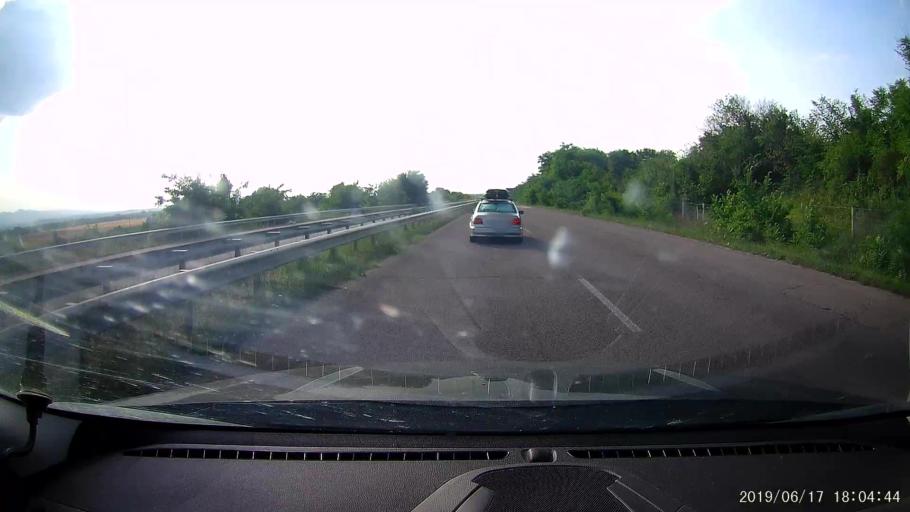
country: BG
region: Khaskovo
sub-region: Obshtina Svilengrad
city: Svilengrad
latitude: 41.7891
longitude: 26.1920
